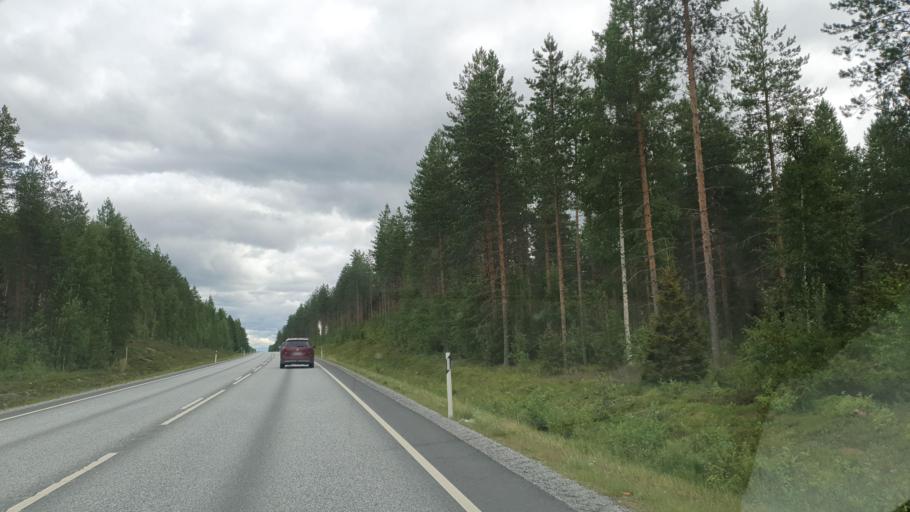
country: FI
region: Northern Savo
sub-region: Ylae-Savo
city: Sonkajaervi
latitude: 63.8972
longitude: 27.4049
